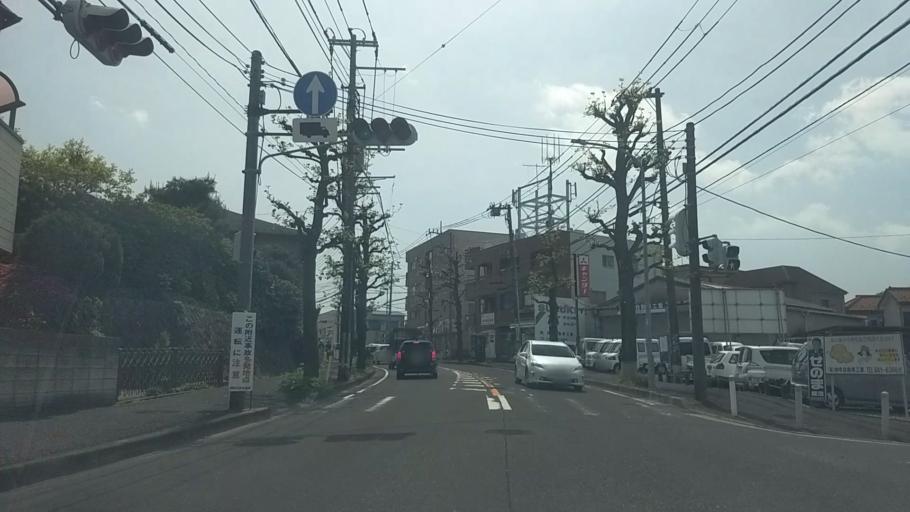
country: JP
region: Kanagawa
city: Yokohama
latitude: 35.3961
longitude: 139.5973
